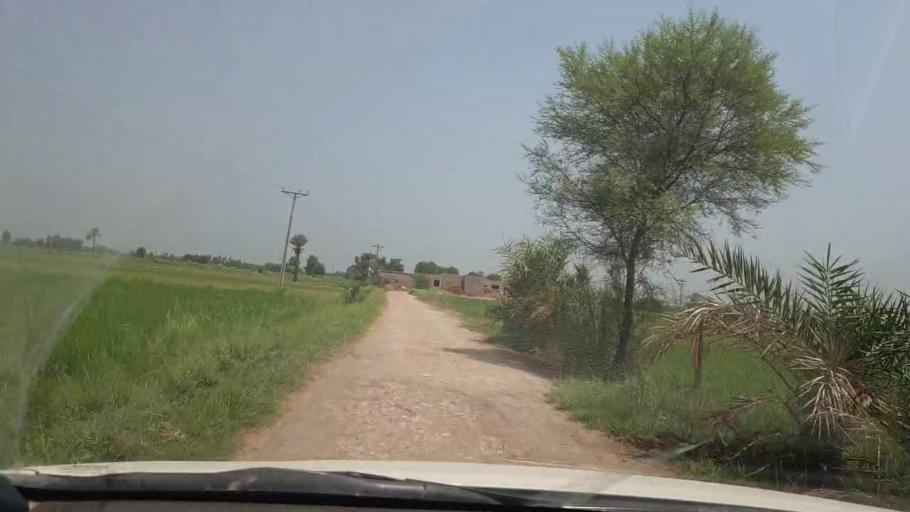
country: PK
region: Sindh
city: Shikarpur
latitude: 27.9329
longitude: 68.6687
